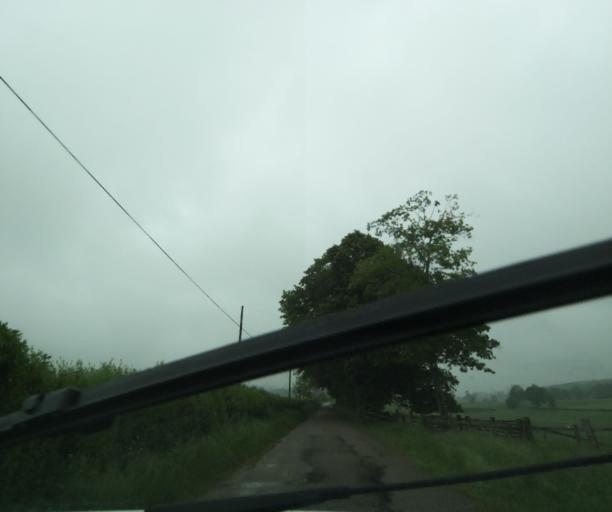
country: FR
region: Bourgogne
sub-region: Departement de Saone-et-Loire
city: Charolles
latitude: 46.3975
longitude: 4.2903
